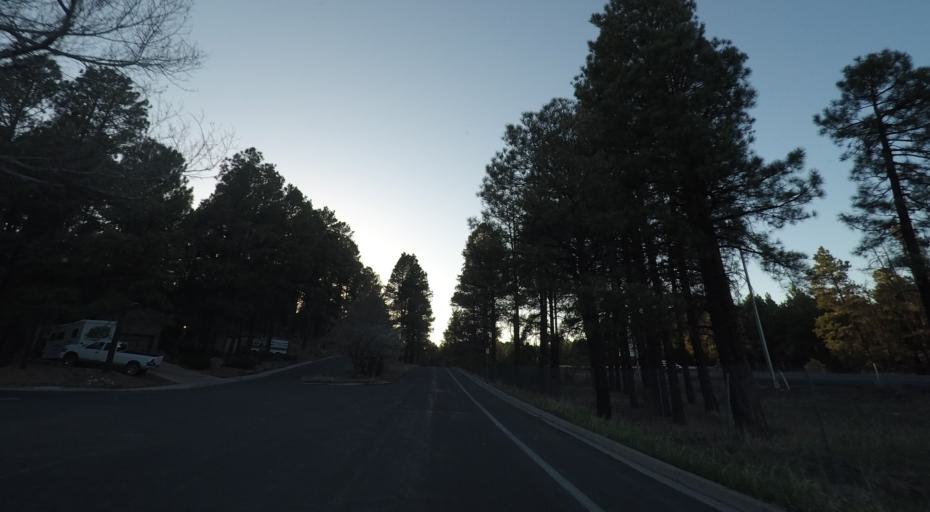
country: US
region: Arizona
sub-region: Coconino County
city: Flagstaff
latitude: 35.1747
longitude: -111.6714
